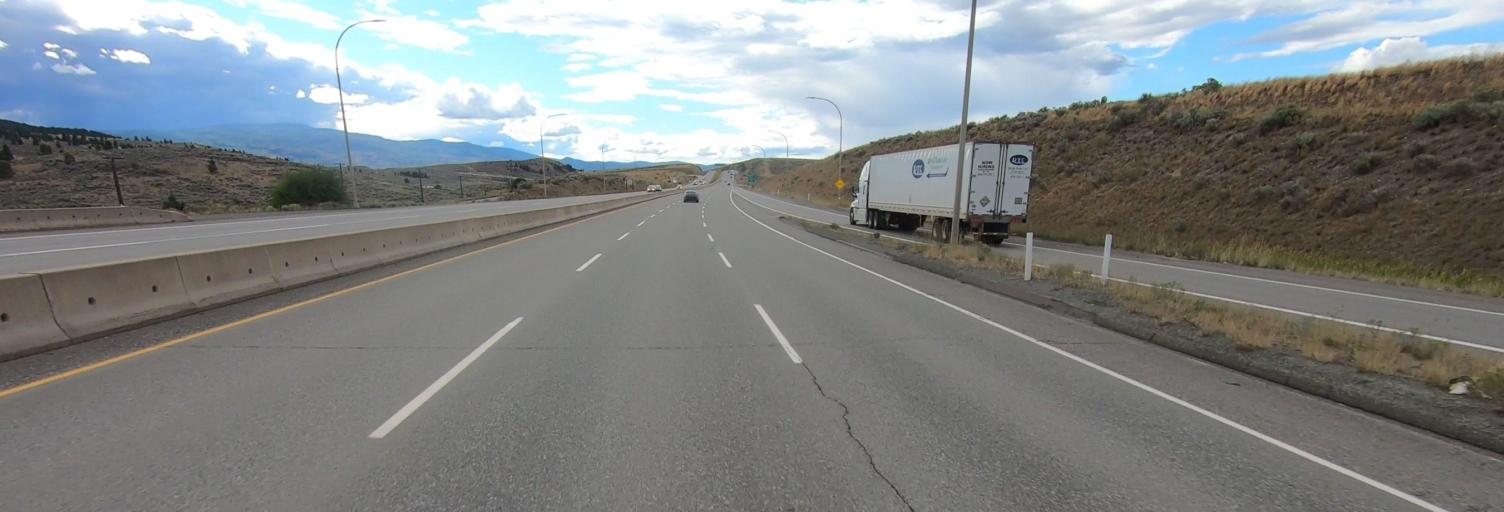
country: CA
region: British Columbia
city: Kamloops
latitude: 50.6665
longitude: -120.4326
